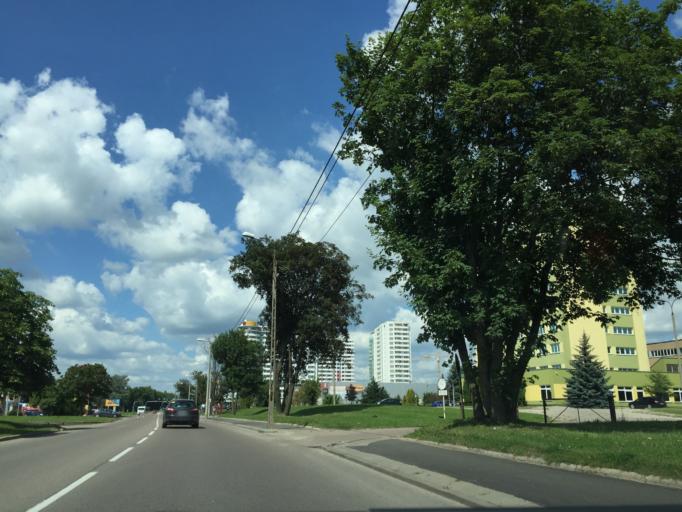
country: PL
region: Podlasie
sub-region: Bialystok
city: Bialystok
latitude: 53.1477
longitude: 23.1569
